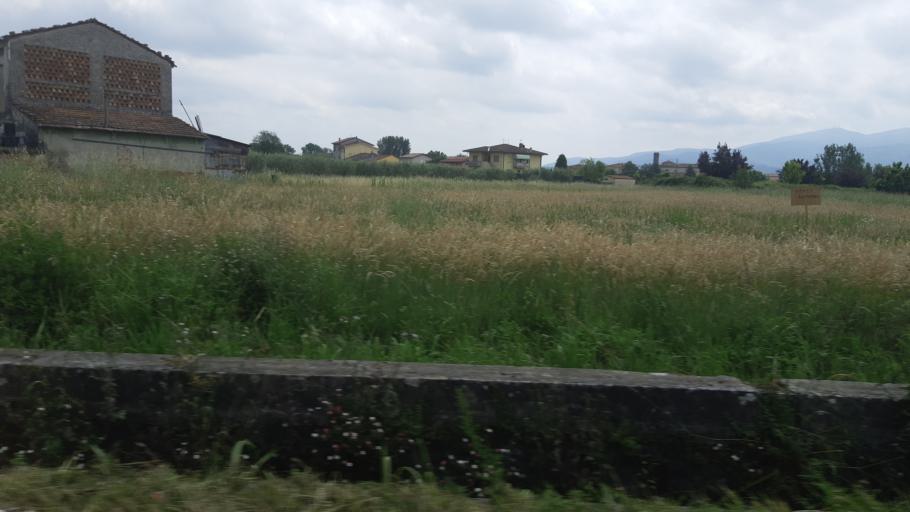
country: IT
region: Tuscany
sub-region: Provincia di Lucca
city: Capannori
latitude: 43.8604
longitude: 10.5476
